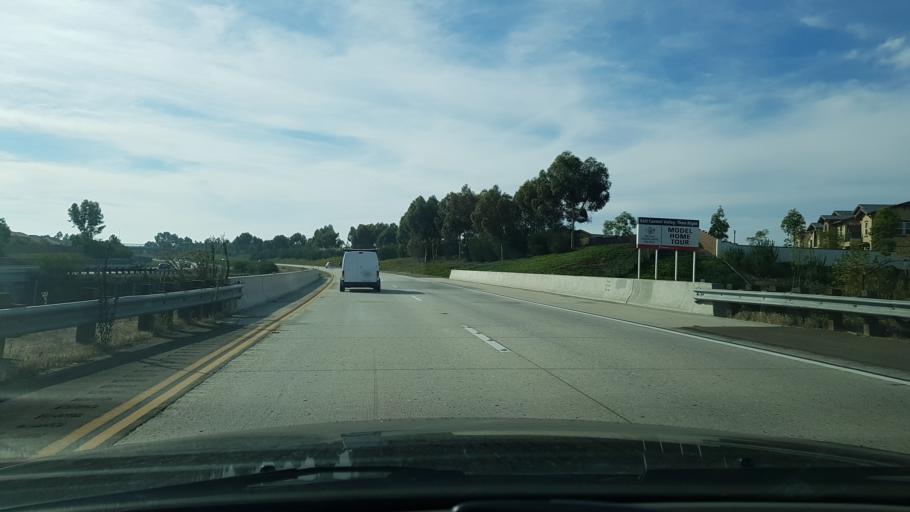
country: US
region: California
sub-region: San Diego County
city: Fairbanks Ranch
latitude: 32.9672
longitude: -117.1712
